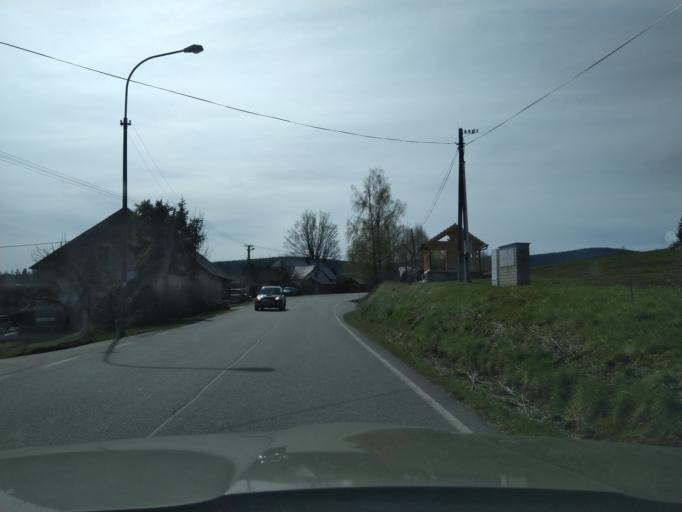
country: CZ
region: Jihocesky
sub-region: Okres Prachatice
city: Stachy
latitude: 49.0865
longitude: 13.6414
